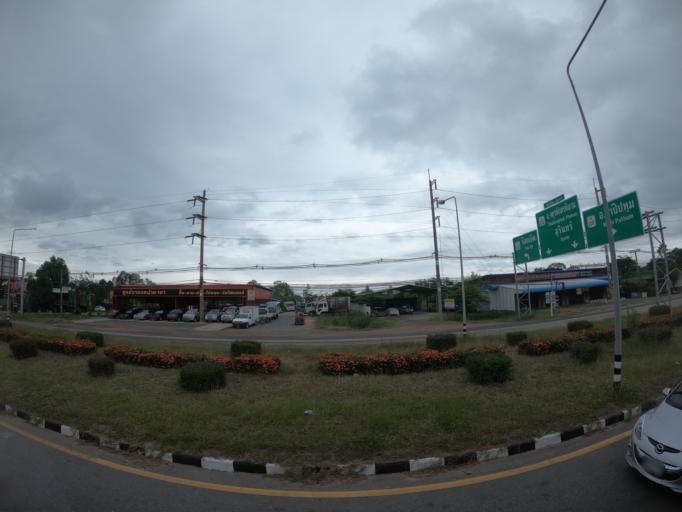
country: TH
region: Roi Et
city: Roi Et
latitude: 16.0432
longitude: 103.6302
